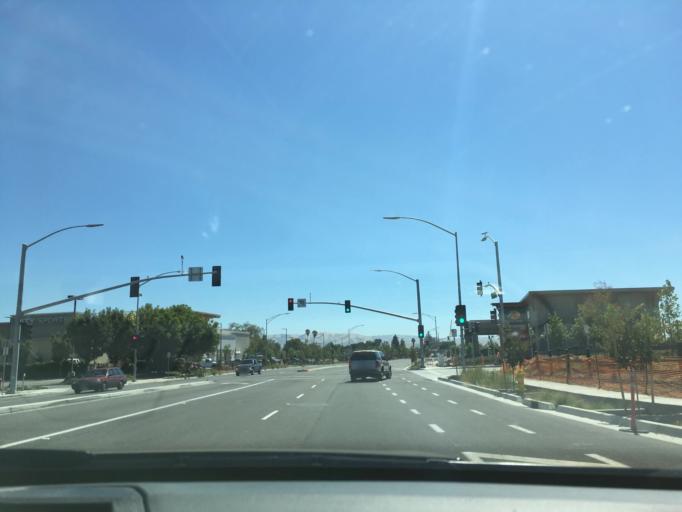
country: US
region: California
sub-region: Santa Clara County
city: Seven Trees
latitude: 37.2591
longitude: -121.8745
